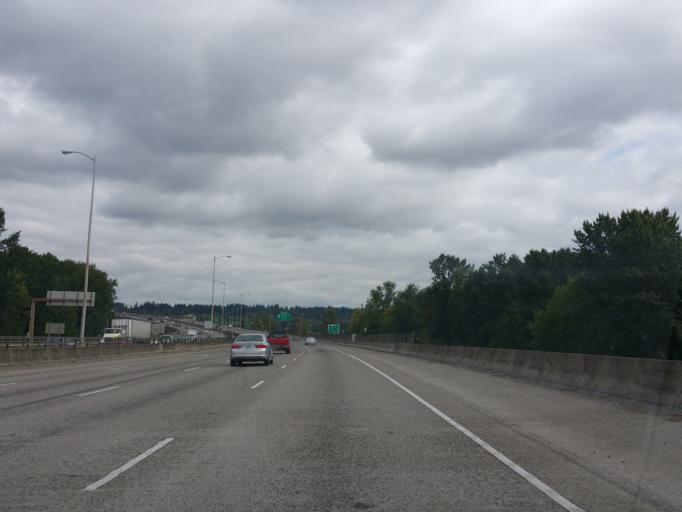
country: US
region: Washington
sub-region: Clark County
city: Mill Plain
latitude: 45.5807
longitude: -122.5434
